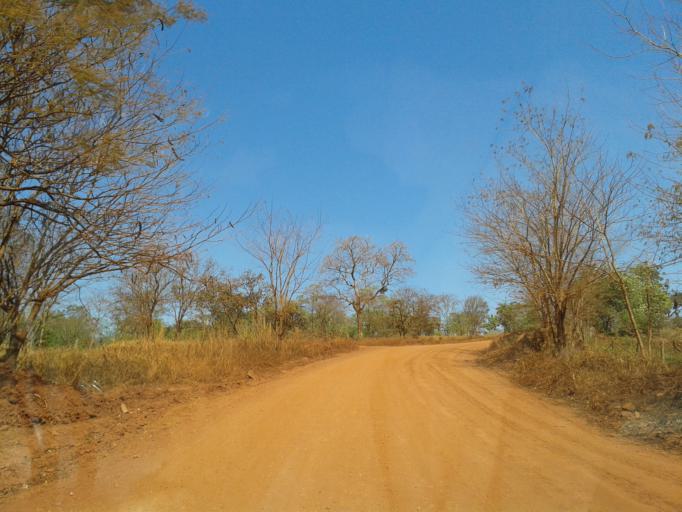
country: BR
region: Minas Gerais
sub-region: Ituiutaba
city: Ituiutaba
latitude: -18.9761
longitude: -49.4207
